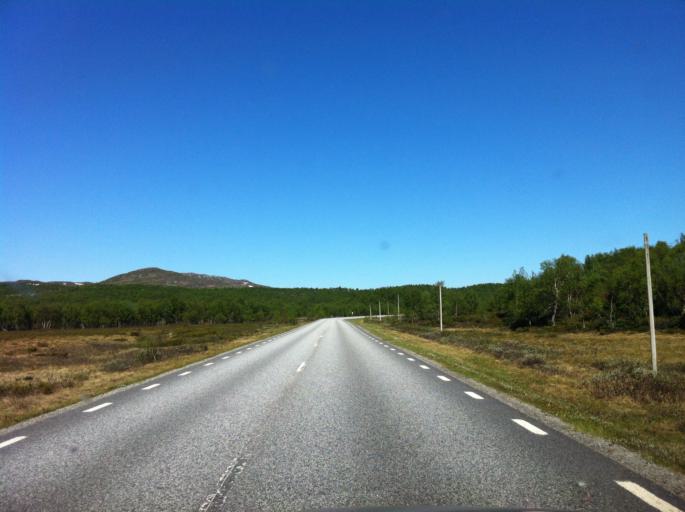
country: NO
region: Sor-Trondelag
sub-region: Tydal
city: Aas
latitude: 62.5951
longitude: 12.1836
